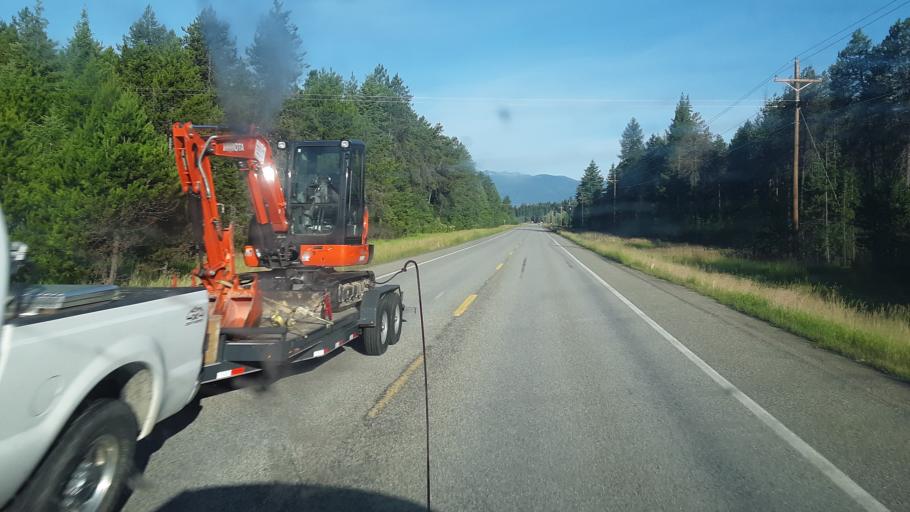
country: US
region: Idaho
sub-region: Boundary County
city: Bonners Ferry
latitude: 48.7290
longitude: -116.2282
